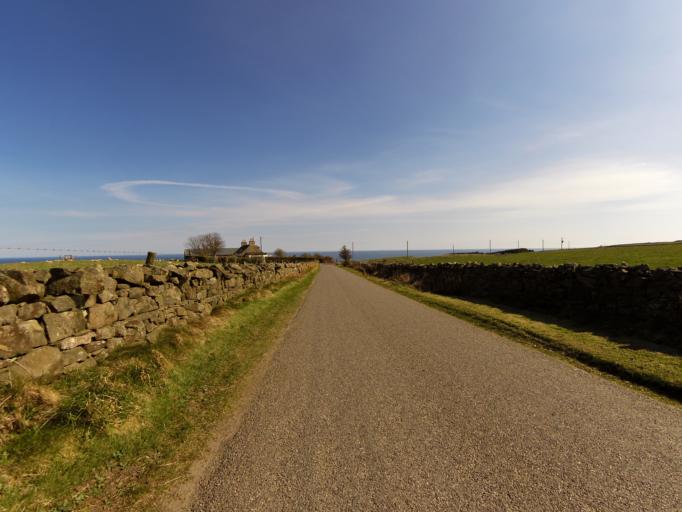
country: GB
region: Scotland
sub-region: Aberdeenshire
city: Portlethen
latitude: 57.0811
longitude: -2.0999
